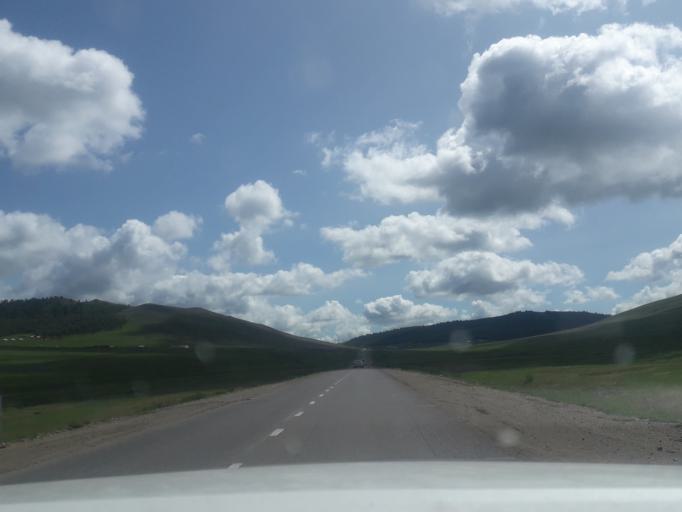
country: MN
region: Central Aimak
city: Ihsueuej
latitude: 48.1657
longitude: 106.4030
